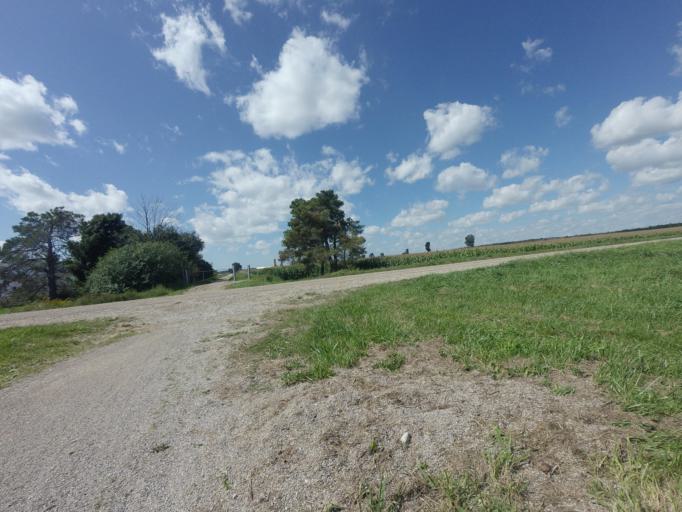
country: CA
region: Ontario
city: Huron East
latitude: 43.6622
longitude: -81.2557
